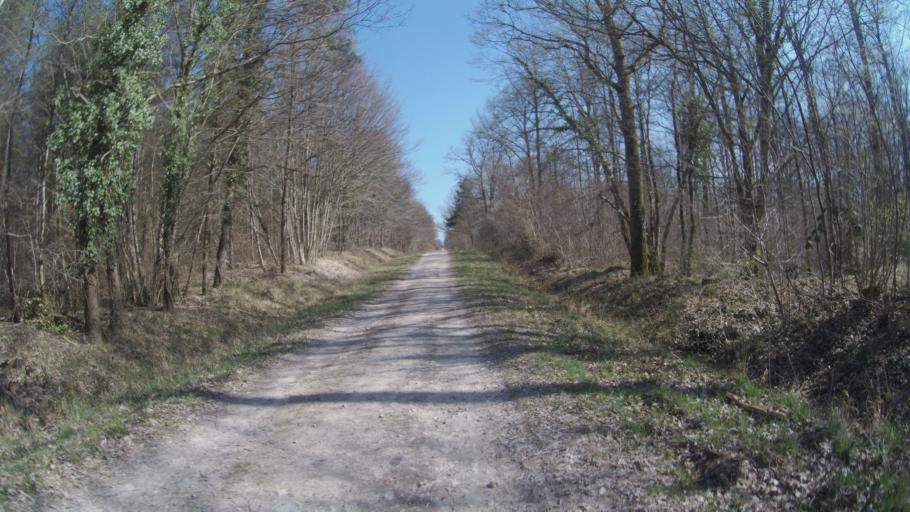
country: FR
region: Centre
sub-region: Departement du Loiret
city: Chanteau
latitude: 47.9503
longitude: 1.9602
